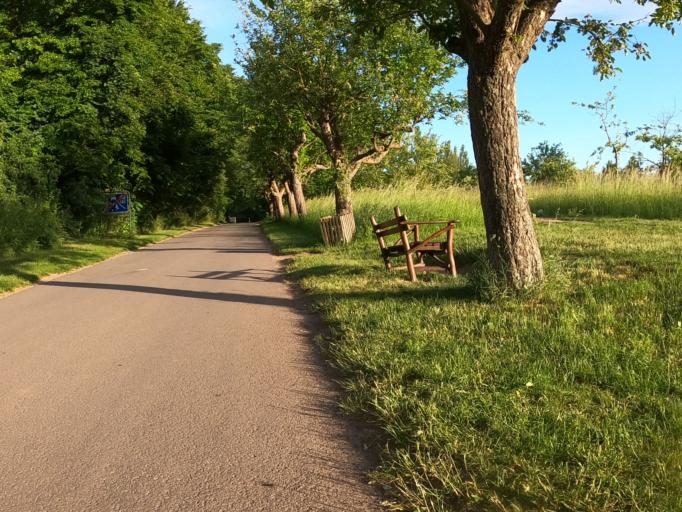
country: DE
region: Hesse
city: Dreieich
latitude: 50.0138
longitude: 8.7313
